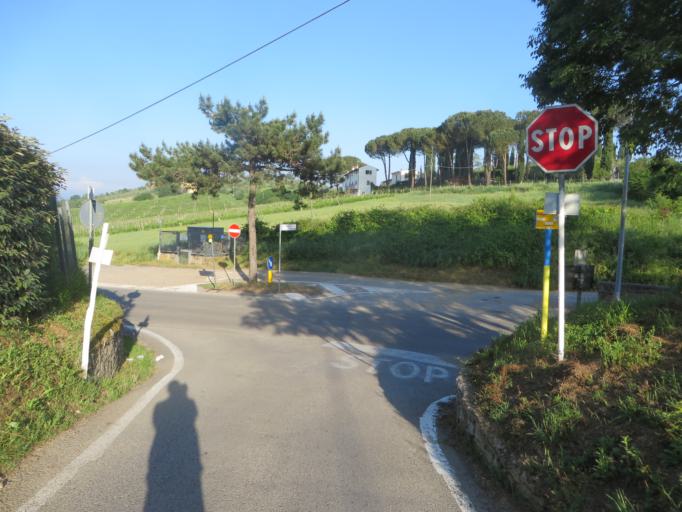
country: IT
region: Tuscany
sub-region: Province of Florence
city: Bagno a Ripoli
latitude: 43.7488
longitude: 11.3177
